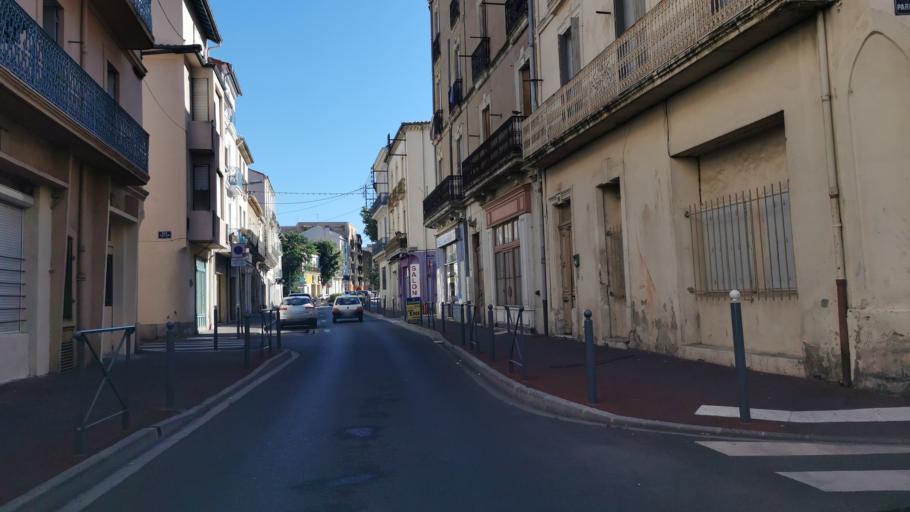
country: FR
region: Languedoc-Roussillon
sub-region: Departement de l'Herault
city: Beziers
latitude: 43.3501
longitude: 3.2186
